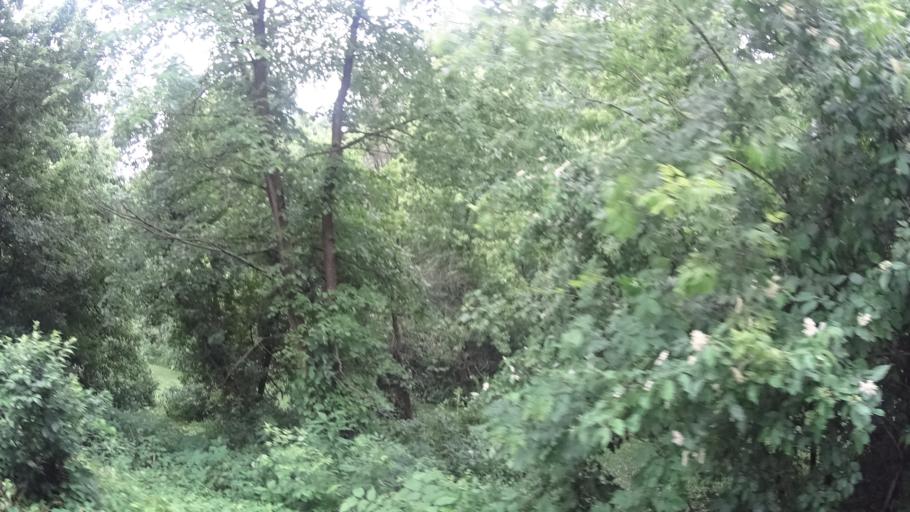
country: US
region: Ohio
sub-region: Erie County
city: Huron
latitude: 41.3515
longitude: -82.5500
